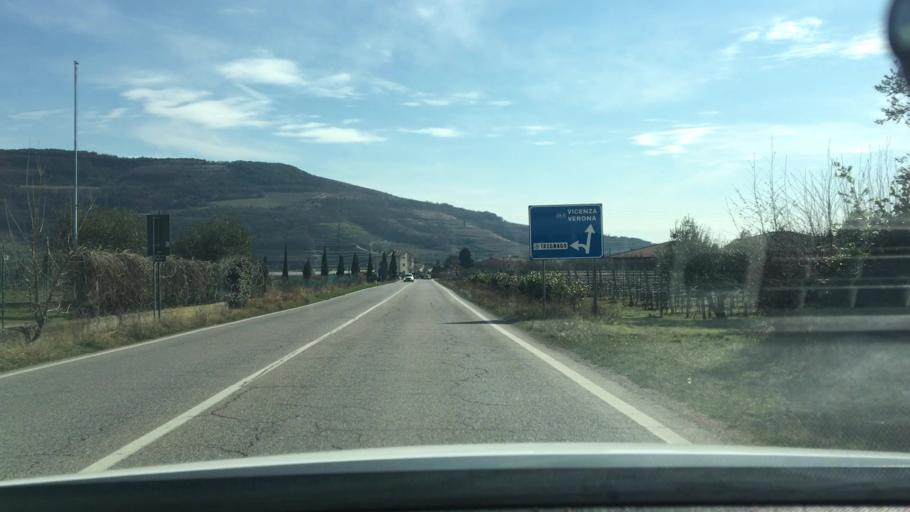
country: IT
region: Veneto
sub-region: Provincia di Verona
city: Tregnago
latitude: 45.5040
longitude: 11.1655
